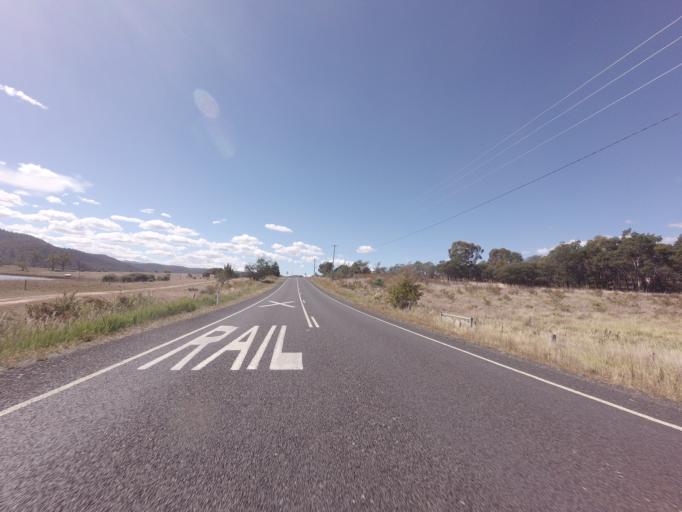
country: AU
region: Tasmania
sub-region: Break O'Day
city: St Helens
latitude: -41.7150
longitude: 147.8363
